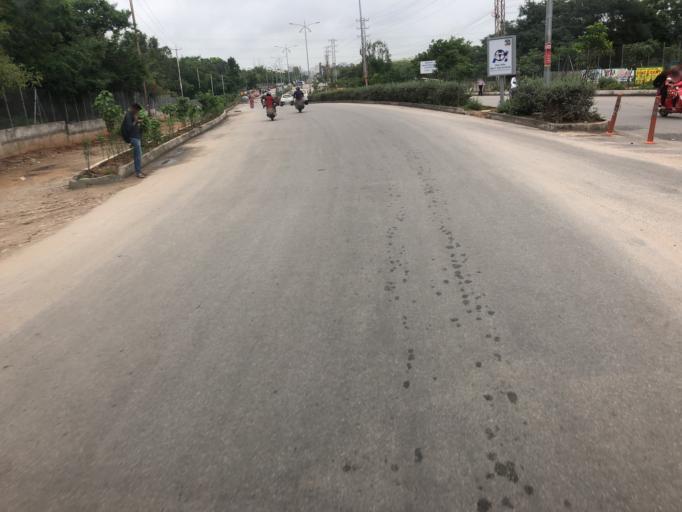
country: IN
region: Telangana
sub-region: Rangareddi
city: Kukatpalli
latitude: 17.4558
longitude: 78.3633
